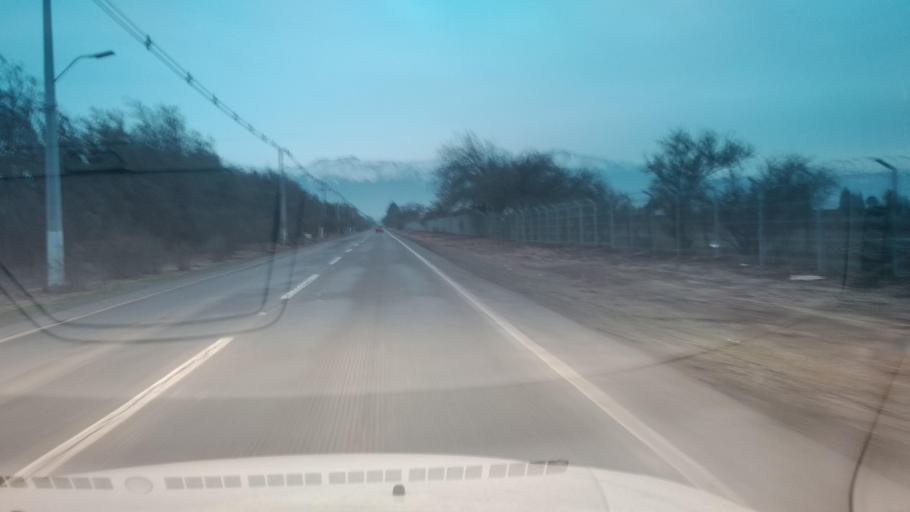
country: CL
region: Santiago Metropolitan
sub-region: Provincia de Chacabuco
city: Chicureo Abajo
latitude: -33.0931
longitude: -70.7168
